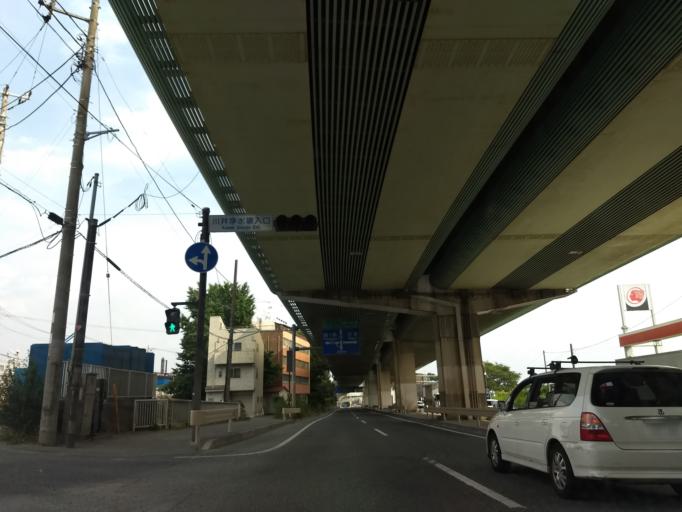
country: JP
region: Kanagawa
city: Minami-rinkan
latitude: 35.5015
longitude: 139.4910
